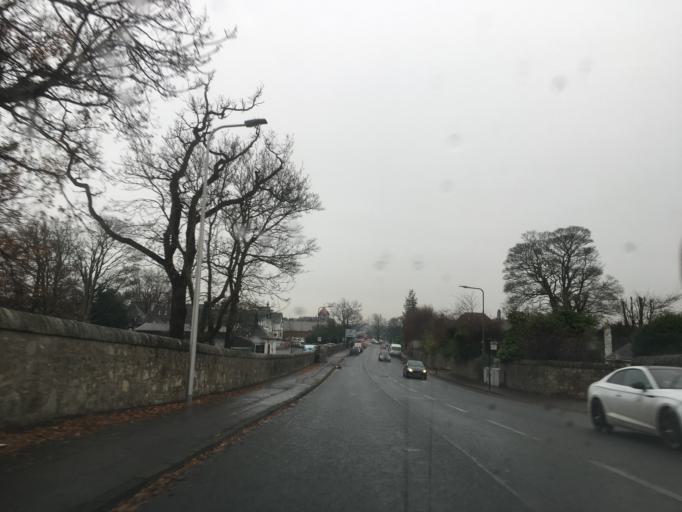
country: GB
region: Scotland
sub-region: Edinburgh
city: Currie
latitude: 55.9638
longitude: -3.3075
